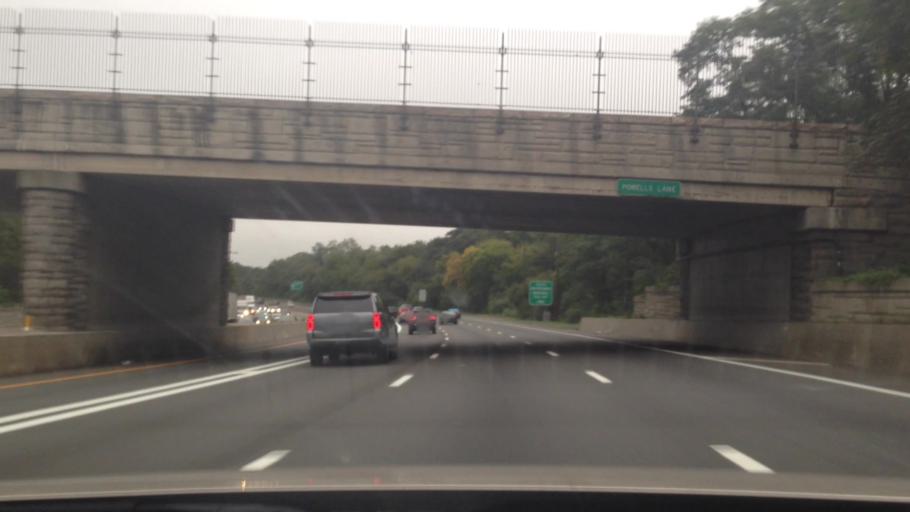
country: US
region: New York
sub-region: Nassau County
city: New Cassel
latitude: 40.7790
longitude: -73.5775
